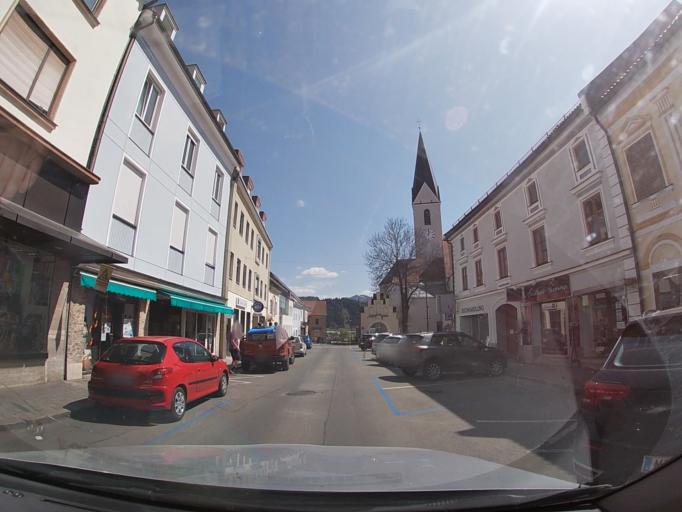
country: AT
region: Styria
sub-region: Politischer Bezirk Murtal
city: Knittelfeld
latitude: 47.2138
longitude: 14.8298
